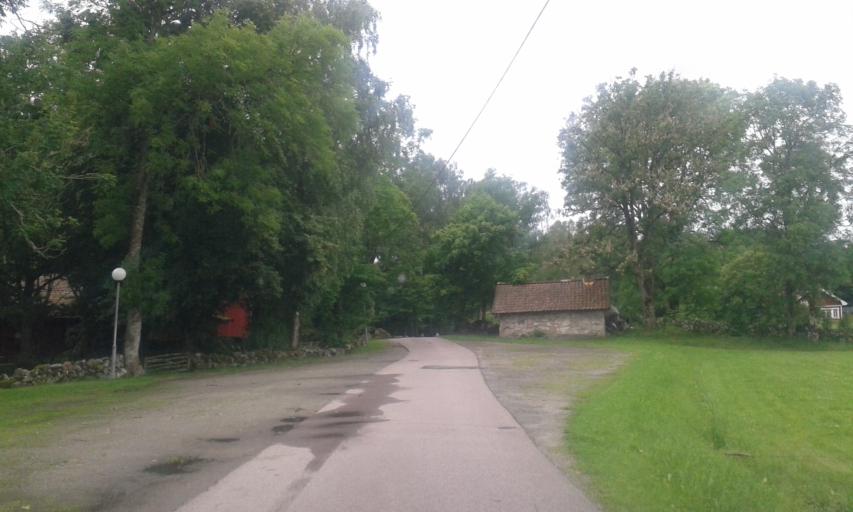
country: SE
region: Vaestra Goetaland
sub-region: Kungalvs Kommun
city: Kode
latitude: 57.8785
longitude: 11.8873
